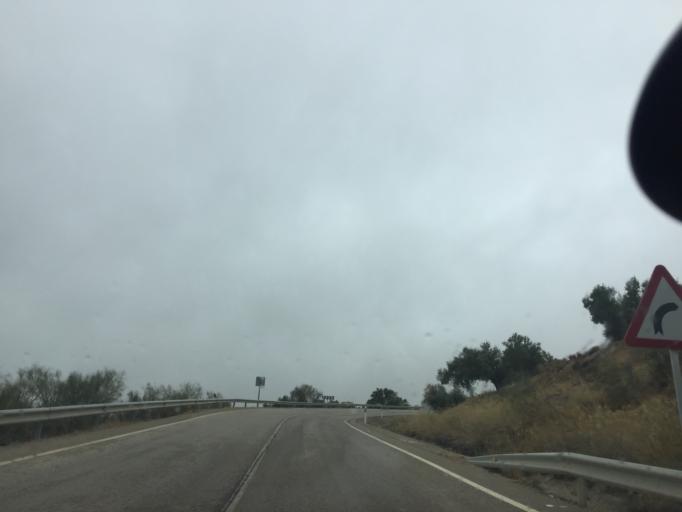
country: ES
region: Andalusia
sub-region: Provincia de Jaen
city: Torres
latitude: 37.8380
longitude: -3.5369
